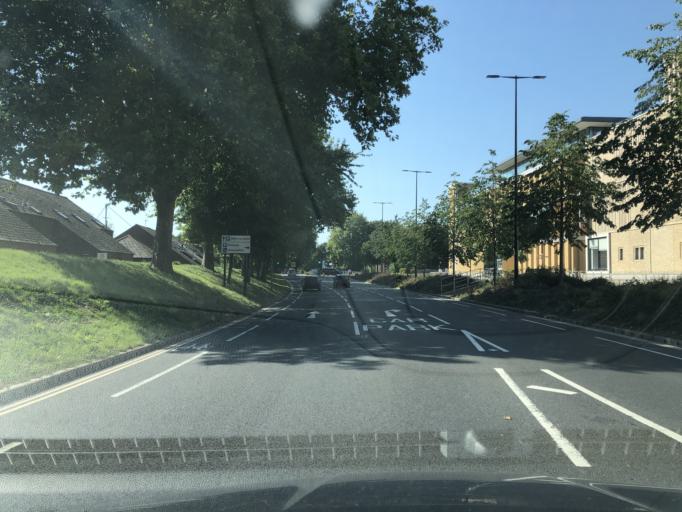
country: GB
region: England
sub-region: Oxfordshire
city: Oxford
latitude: 51.7485
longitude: -1.2618
